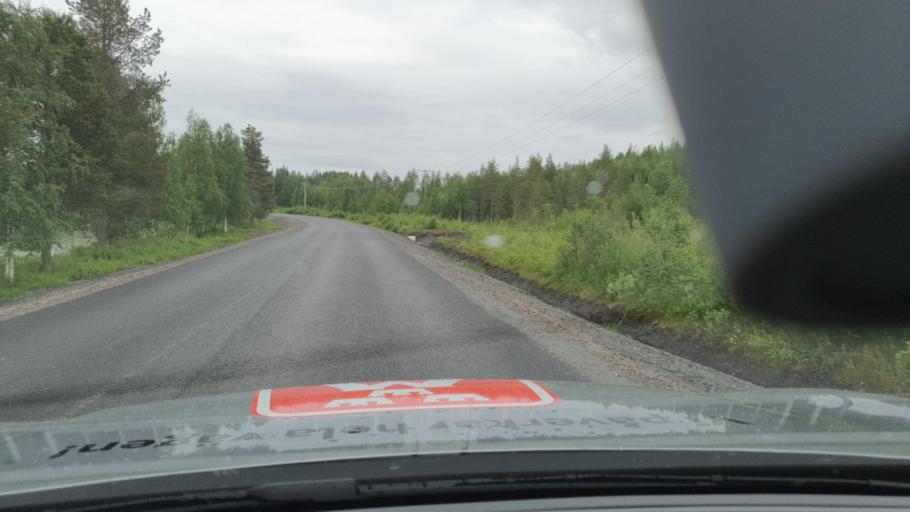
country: SE
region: Norrbotten
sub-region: Pajala Kommun
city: Pajala
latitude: 66.7382
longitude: 23.1689
